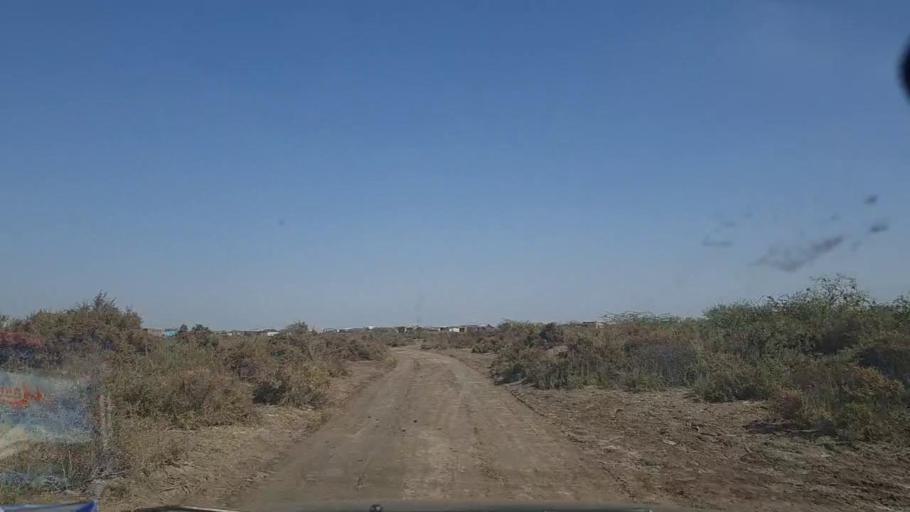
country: PK
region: Sindh
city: Chuhar Jamali
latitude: 24.2729
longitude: 67.7572
